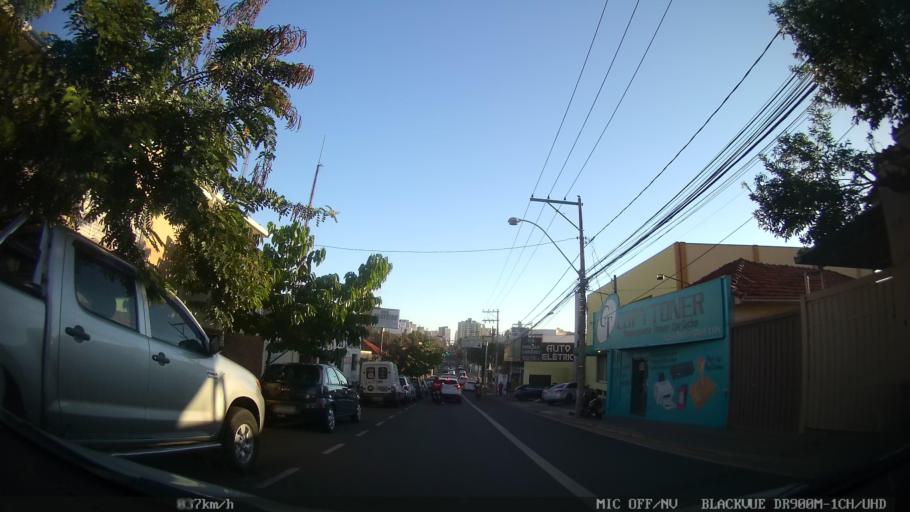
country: BR
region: Sao Paulo
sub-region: Sao Jose Do Rio Preto
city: Sao Jose do Rio Preto
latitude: -20.8059
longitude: -49.3762
